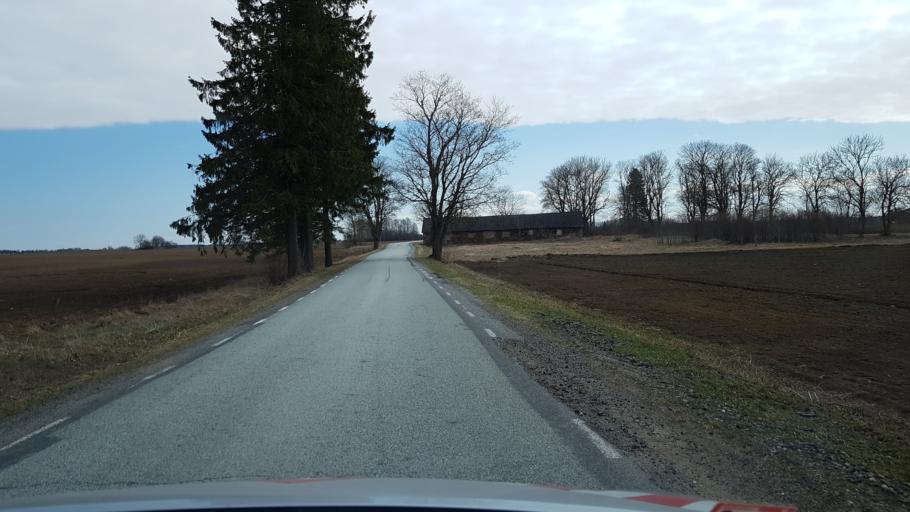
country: EE
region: Laeaene-Virumaa
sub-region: Haljala vald
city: Haljala
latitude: 59.4243
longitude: 26.2265
